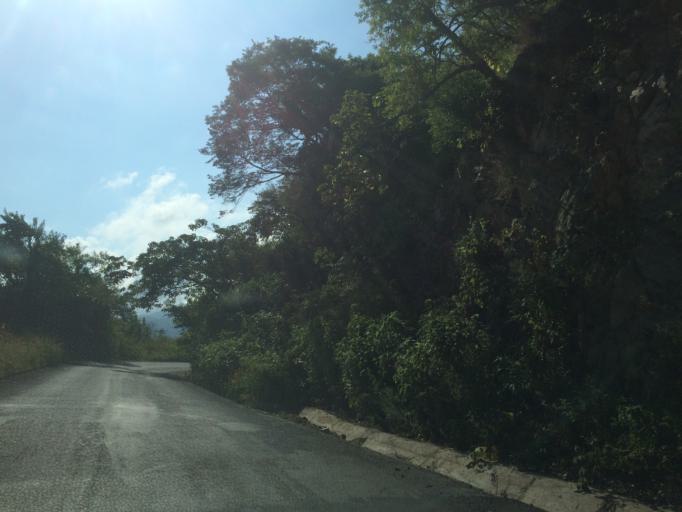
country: MX
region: Nayarit
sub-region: Ahuacatlan
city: Ahuacatlan
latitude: 21.0183
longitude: -104.4762
